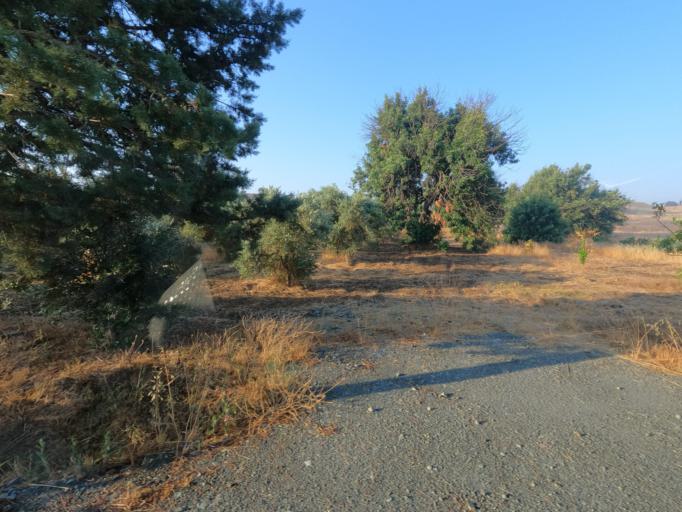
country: CY
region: Larnaka
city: Mosfiloti
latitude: 34.9734
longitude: 33.4369
